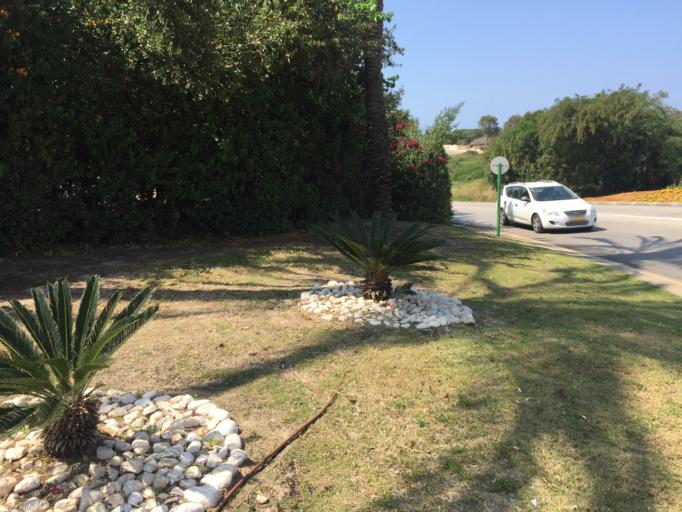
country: IL
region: Haifa
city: Qesarya
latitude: 32.4899
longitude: 34.9032
